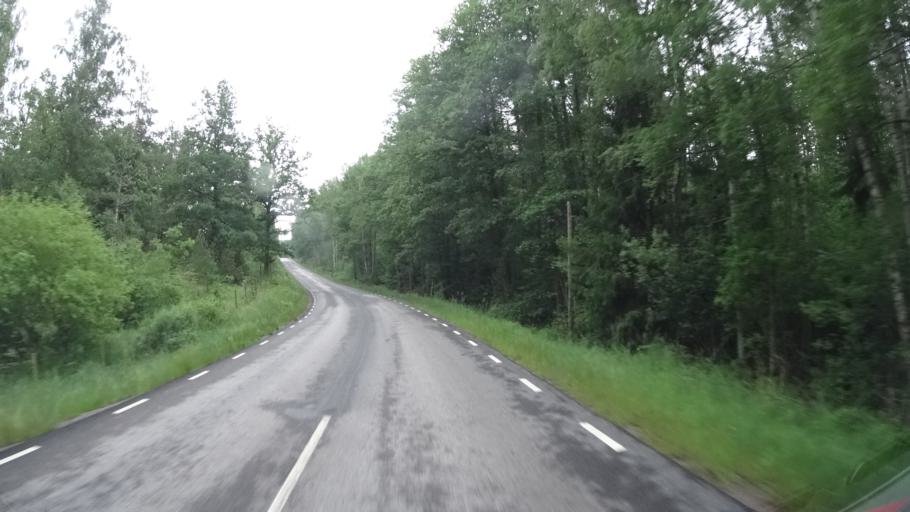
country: SE
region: Kalmar
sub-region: Oskarshamns Kommun
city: Oskarshamn
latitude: 57.3671
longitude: 16.2280
